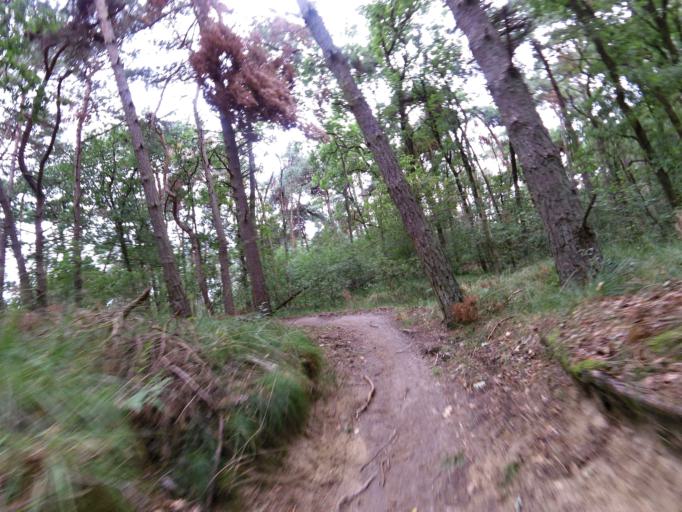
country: NL
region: North Brabant
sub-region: Gemeente Loon op Zand
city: Loon op Zand
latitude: 51.6559
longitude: 5.1254
